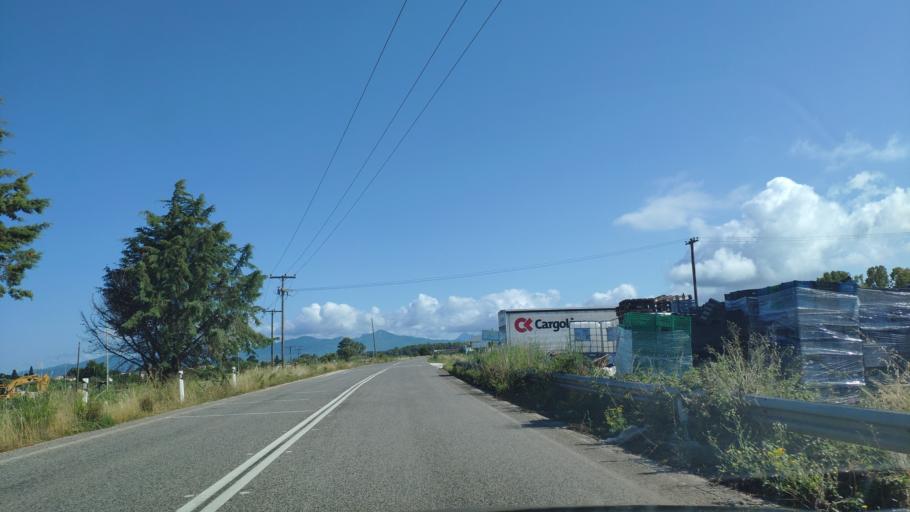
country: GR
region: Epirus
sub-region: Nomos Prevezis
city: Preveza
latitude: 38.9881
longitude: 20.7138
